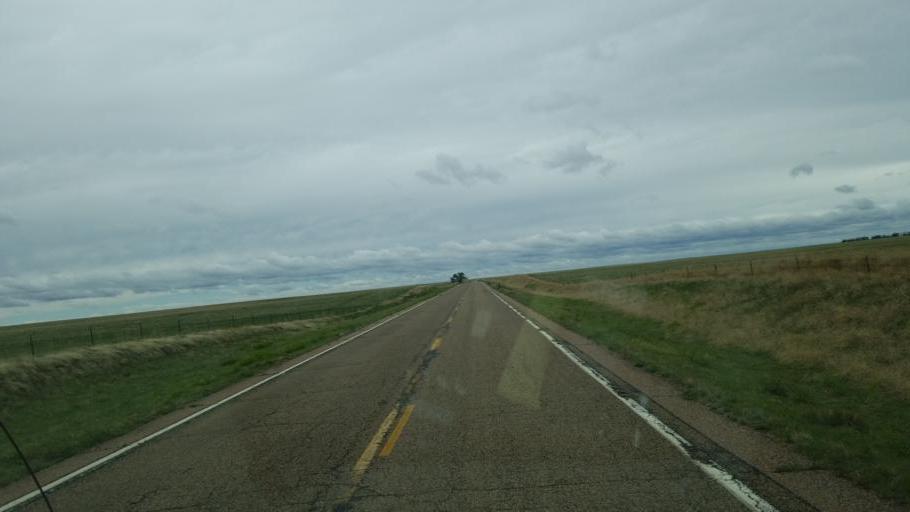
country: US
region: Colorado
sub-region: Lincoln County
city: Hugo
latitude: 38.8523
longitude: -103.7246
